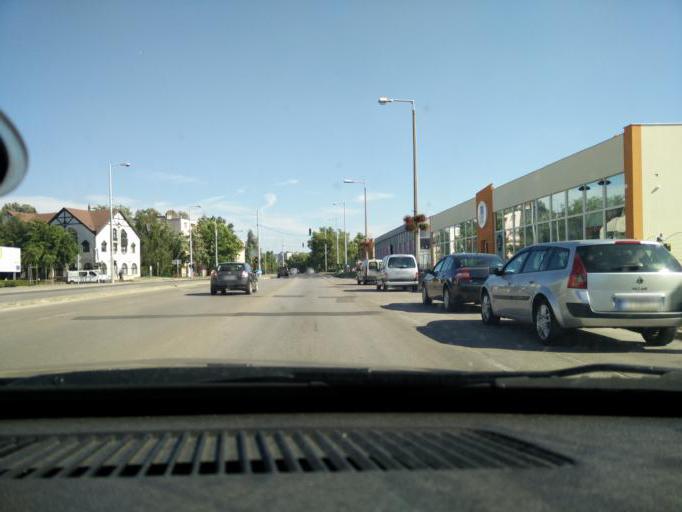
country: HU
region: Komarom-Esztergom
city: Tatabanya
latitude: 47.5811
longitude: 18.3984
